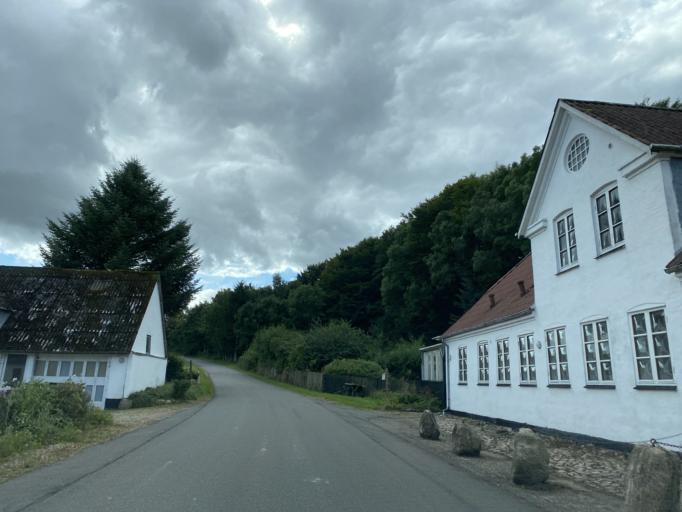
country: DK
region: Central Jutland
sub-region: Horsens Kommune
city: Horsens
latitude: 55.9554
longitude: 9.8561
